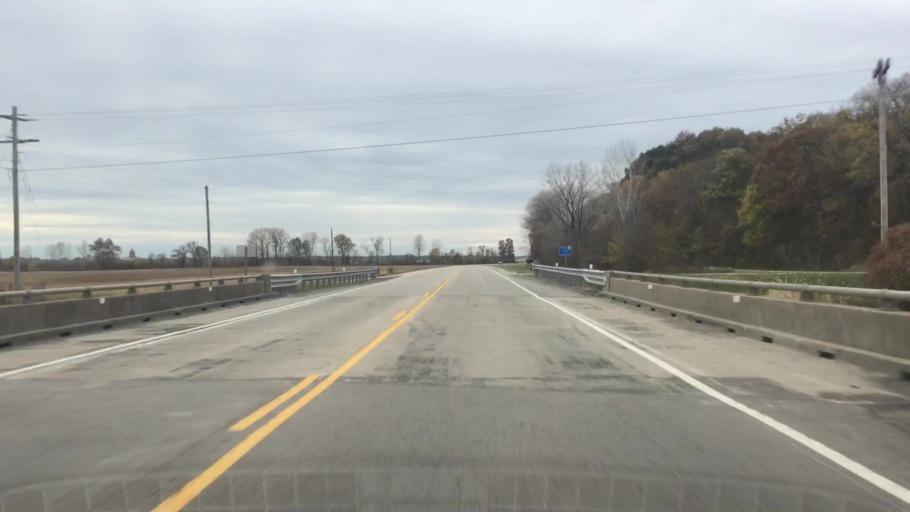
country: US
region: Missouri
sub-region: Callaway County
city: Holts Summit
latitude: 38.5831
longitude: -92.1110
